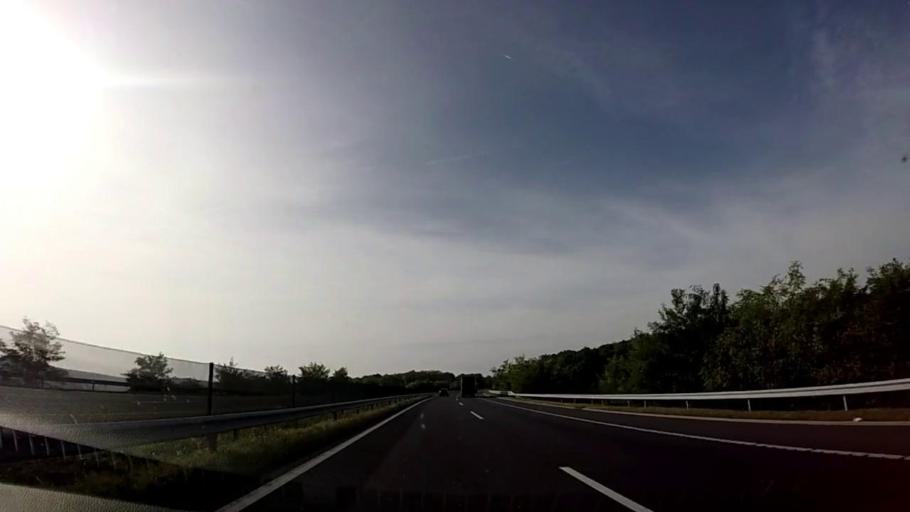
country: HU
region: Somogy
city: Zamardi
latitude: 46.8371
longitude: 17.9503
